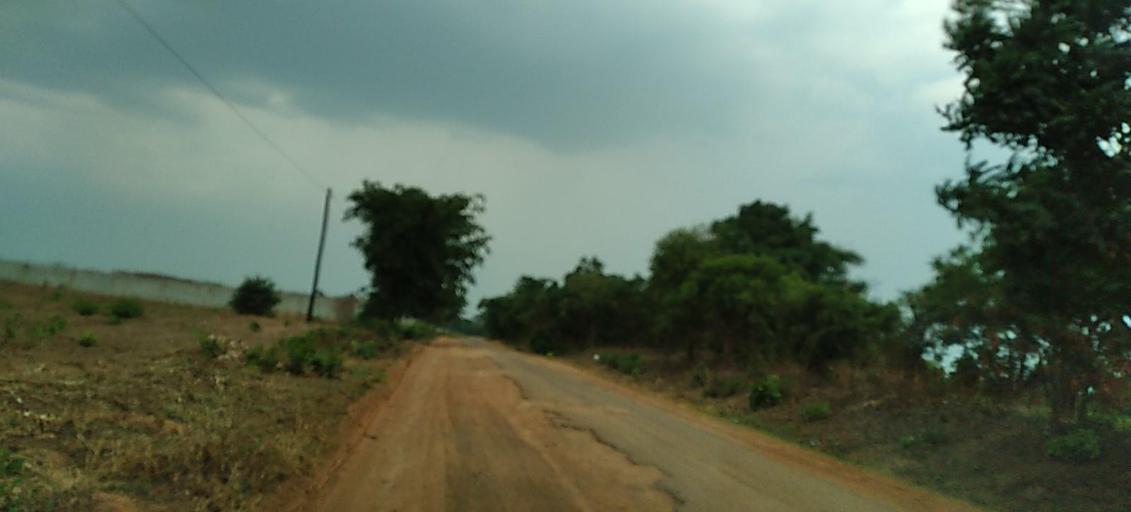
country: ZM
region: Copperbelt
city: Kalulushi
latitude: -12.8882
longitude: 28.1212
